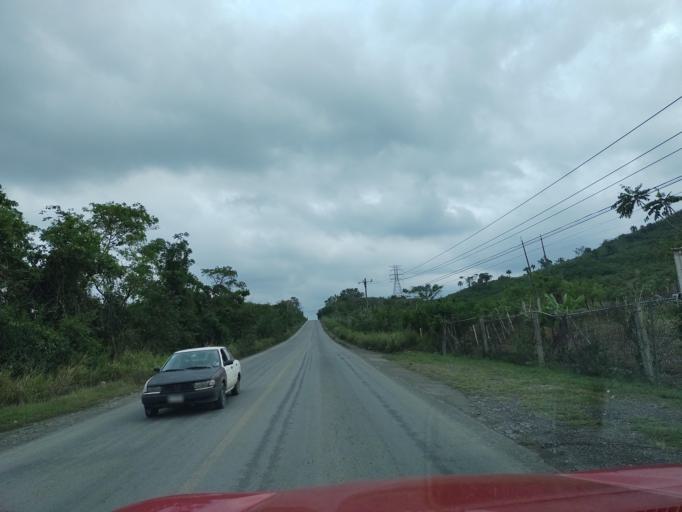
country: MX
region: Veracruz
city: Coatzintla
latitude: 20.4535
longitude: -97.4121
